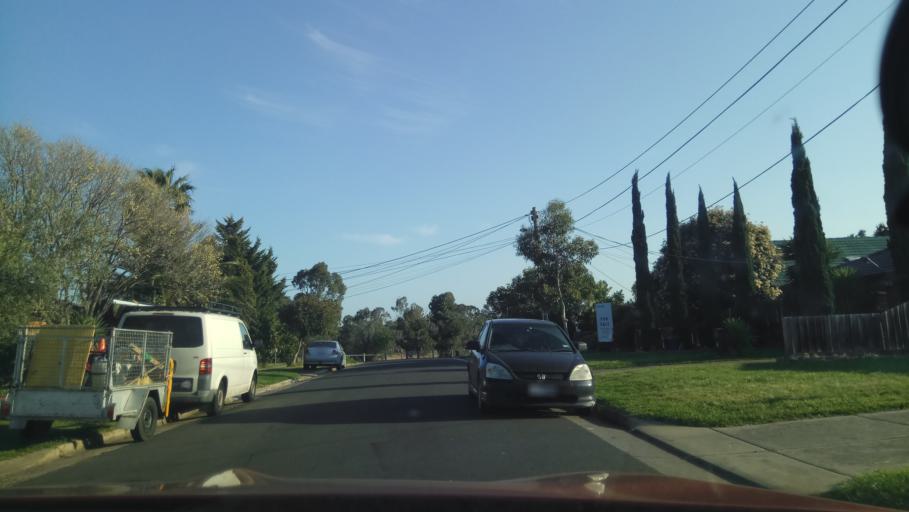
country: AU
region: Victoria
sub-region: Hobsons Bay
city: Laverton
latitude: -37.8718
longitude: 144.7624
